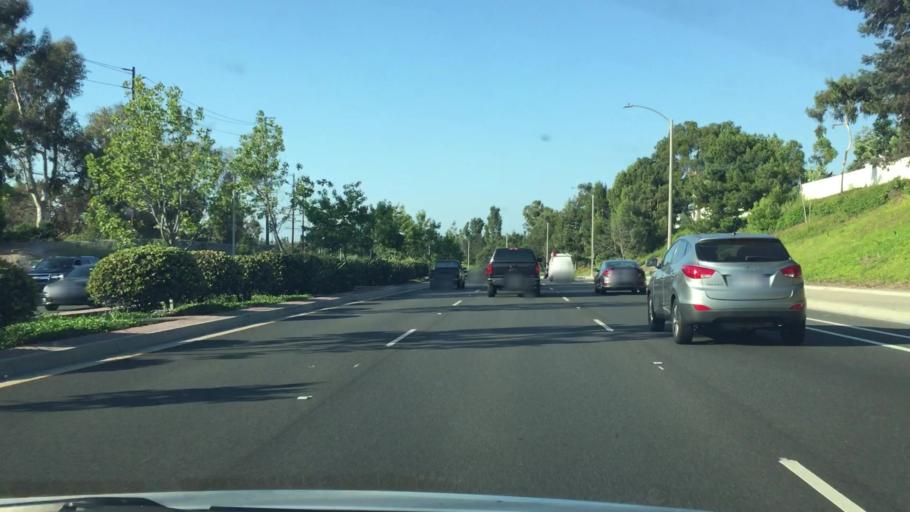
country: US
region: California
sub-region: Orange County
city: San Joaquin Hills
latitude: 33.6187
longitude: -117.8624
